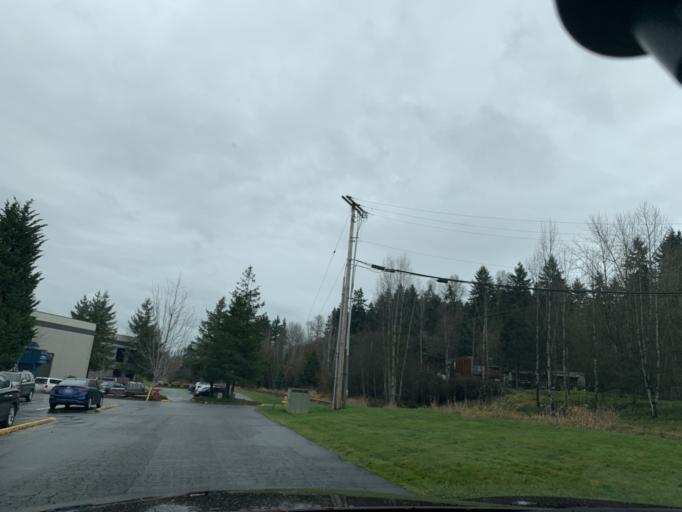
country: US
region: Washington
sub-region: King County
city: Woodinville
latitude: 47.7387
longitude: -122.1558
